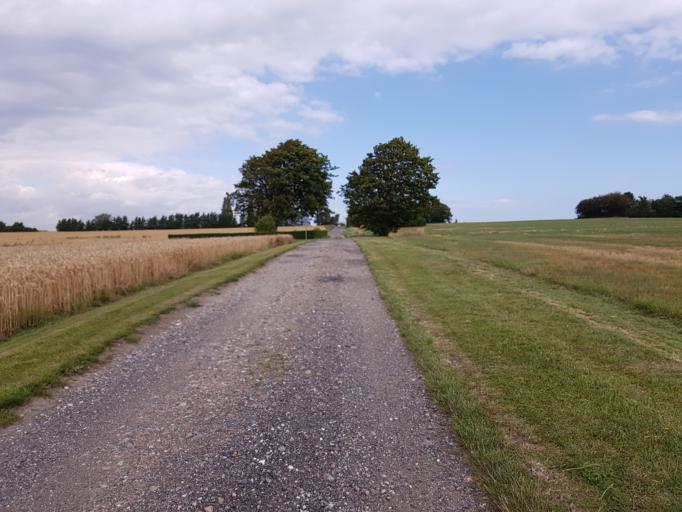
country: DK
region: Zealand
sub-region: Guldborgsund Kommune
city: Nykobing Falster
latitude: 54.5812
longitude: 11.9430
